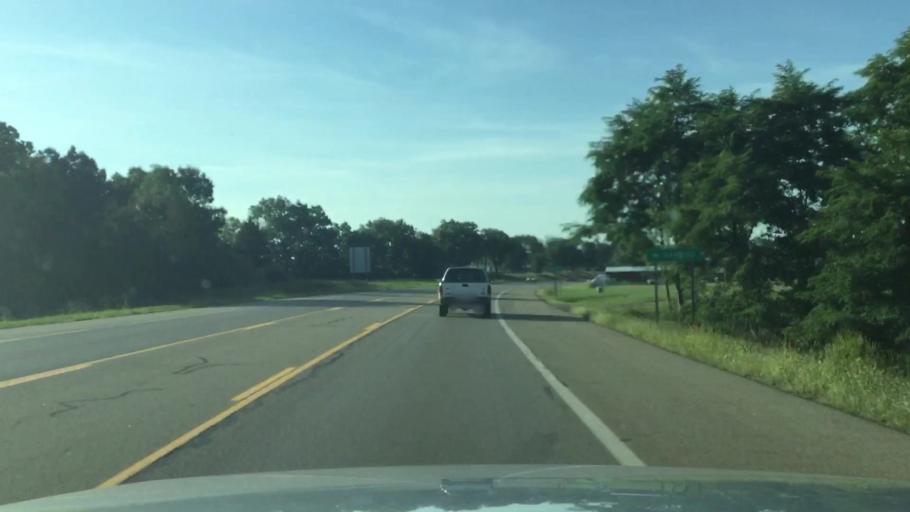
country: US
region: Michigan
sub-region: Jackson County
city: Vandercook Lake
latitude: 42.1814
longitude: -84.3660
